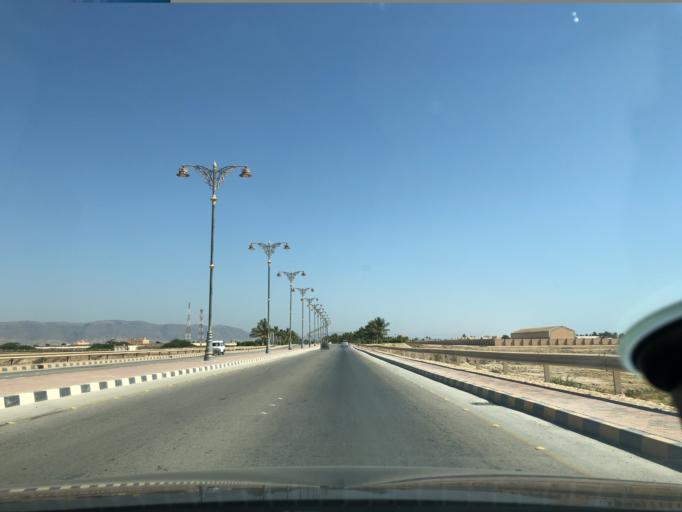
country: OM
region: Zufar
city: Salalah
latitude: 17.0259
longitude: 54.1744
